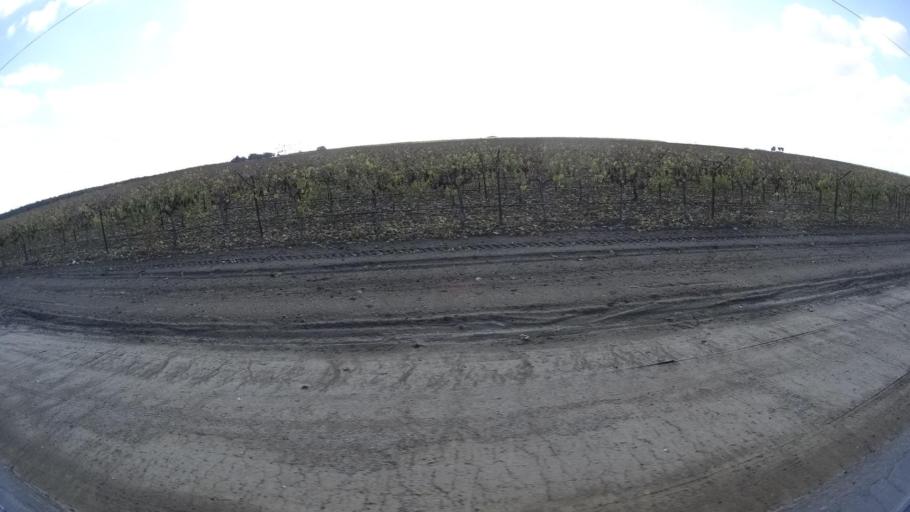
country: US
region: California
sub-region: Kern County
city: McFarland
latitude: 35.6888
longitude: -119.2713
